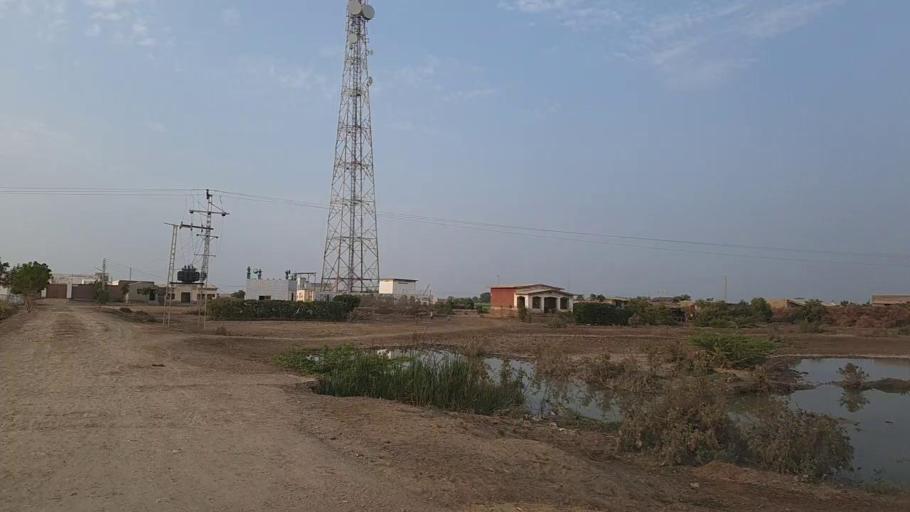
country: PK
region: Sindh
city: Mirwah Gorchani
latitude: 25.3176
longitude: 69.1975
